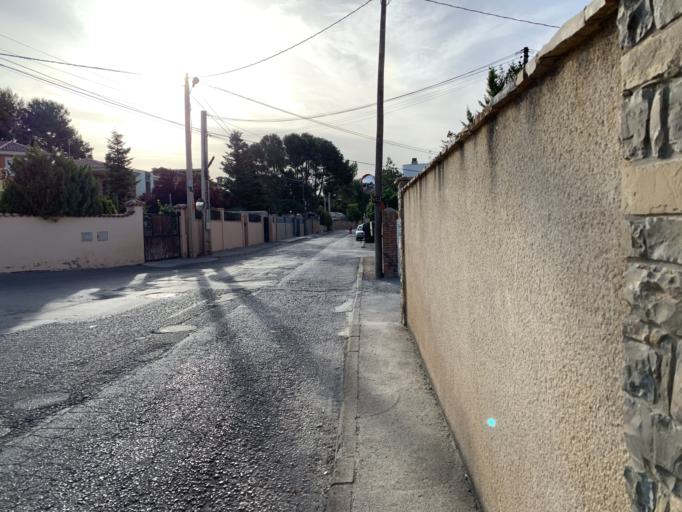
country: ES
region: Aragon
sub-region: Provincia de Teruel
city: Teruel
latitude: 40.3539
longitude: -1.1142
